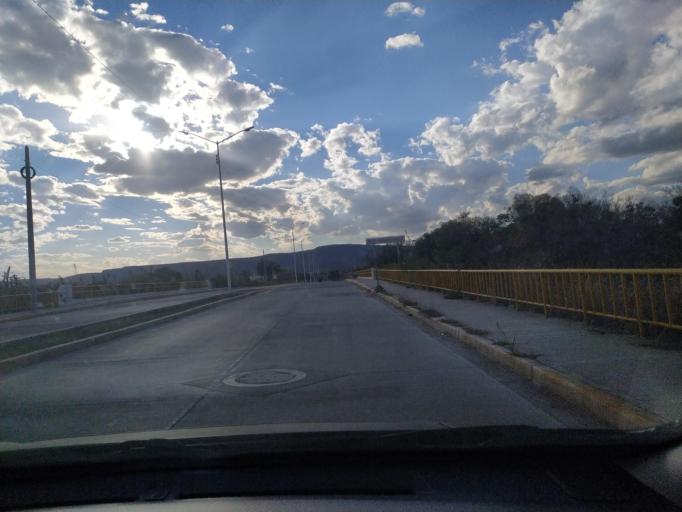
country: LA
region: Oudomxai
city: Muang La
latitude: 21.0177
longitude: 101.8389
